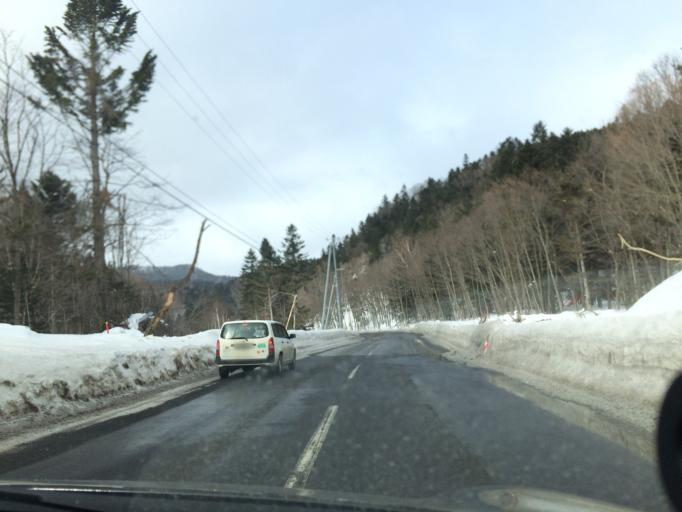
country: JP
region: Hokkaido
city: Shimo-furano
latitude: 43.0820
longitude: 142.6747
